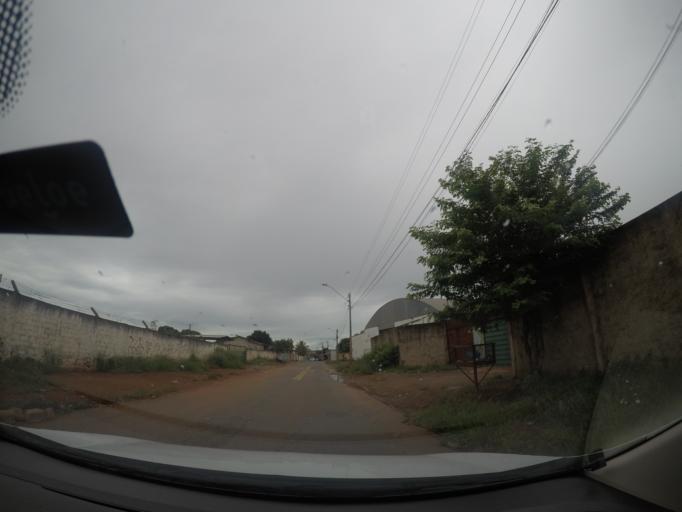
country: BR
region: Goias
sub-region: Goiania
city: Goiania
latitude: -16.6497
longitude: -49.3195
